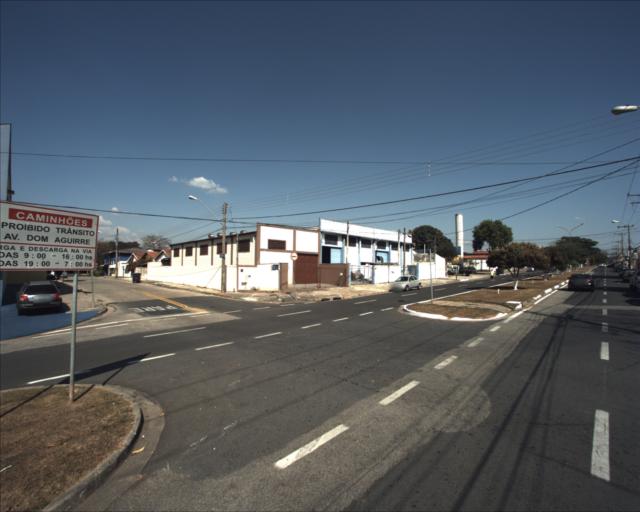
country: BR
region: Sao Paulo
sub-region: Sorocaba
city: Sorocaba
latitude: -23.4708
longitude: -47.4431
